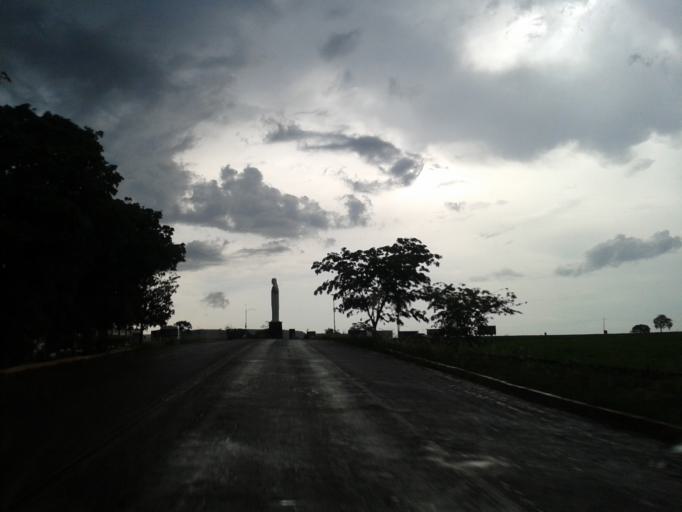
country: BR
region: Goias
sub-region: Quirinopolis
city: Quirinopolis
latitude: -18.4405
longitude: -50.4163
